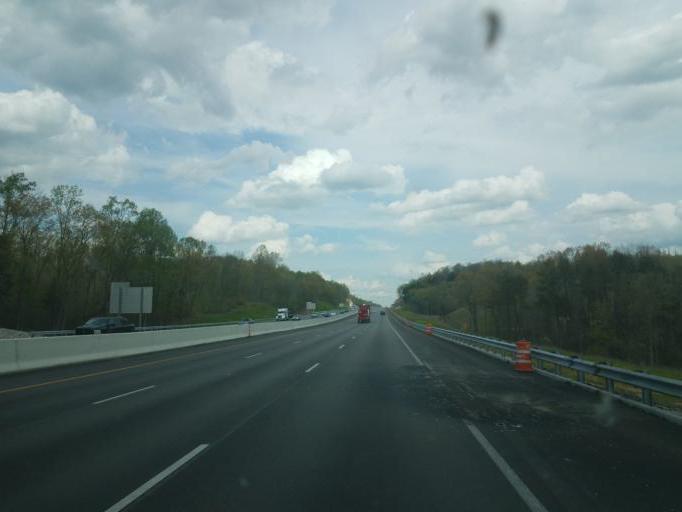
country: US
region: Kentucky
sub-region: Hart County
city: Munfordville
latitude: 37.2997
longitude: -85.9016
